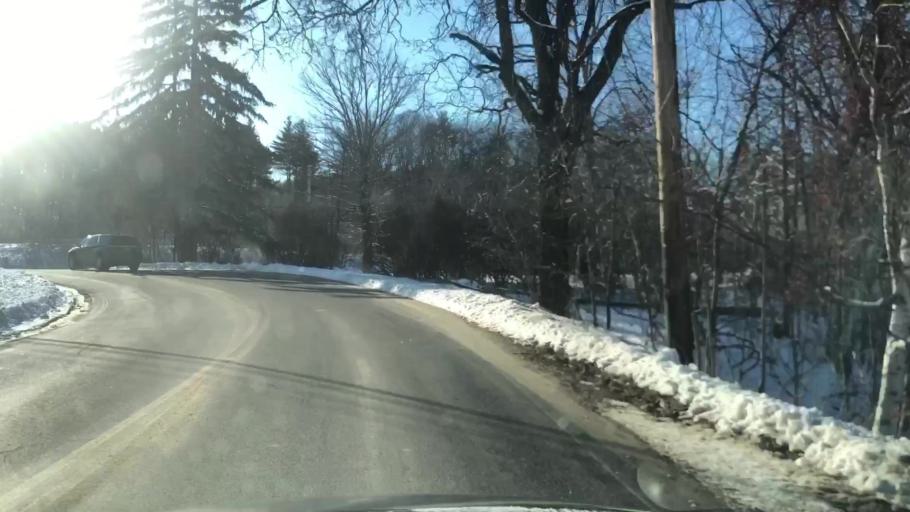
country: US
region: New Hampshire
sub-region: Hillsborough County
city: Wilton
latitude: 42.8396
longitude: -71.7049
